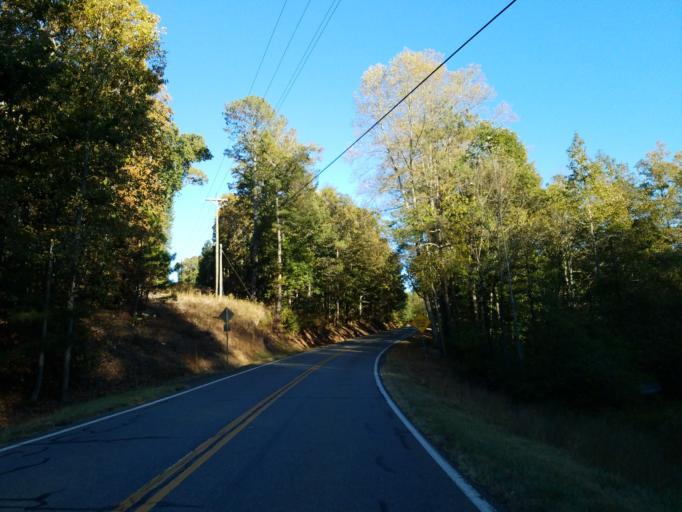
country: US
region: Georgia
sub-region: Pickens County
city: Nelson
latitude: 34.4159
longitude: -84.2625
